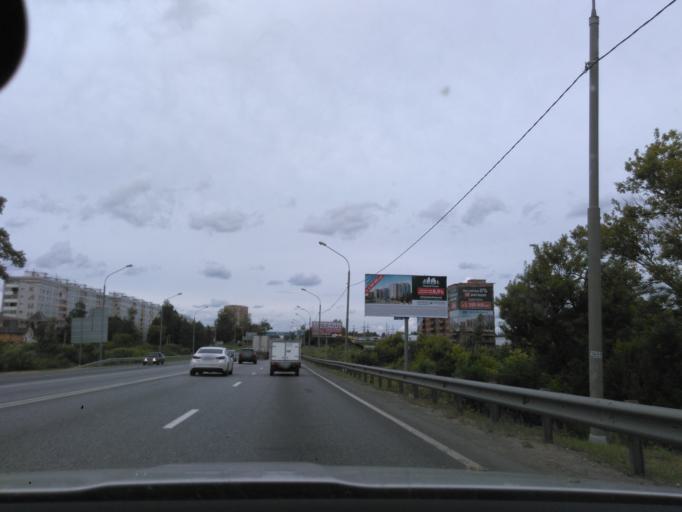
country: RU
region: Moskovskaya
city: Klin
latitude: 56.3176
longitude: 36.7672
